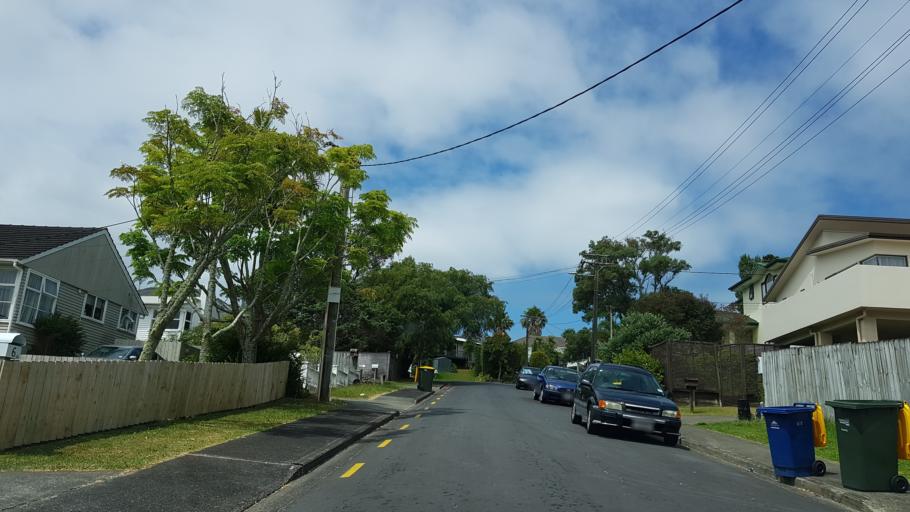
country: NZ
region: Auckland
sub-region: Auckland
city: North Shore
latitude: -36.7728
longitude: 174.7182
